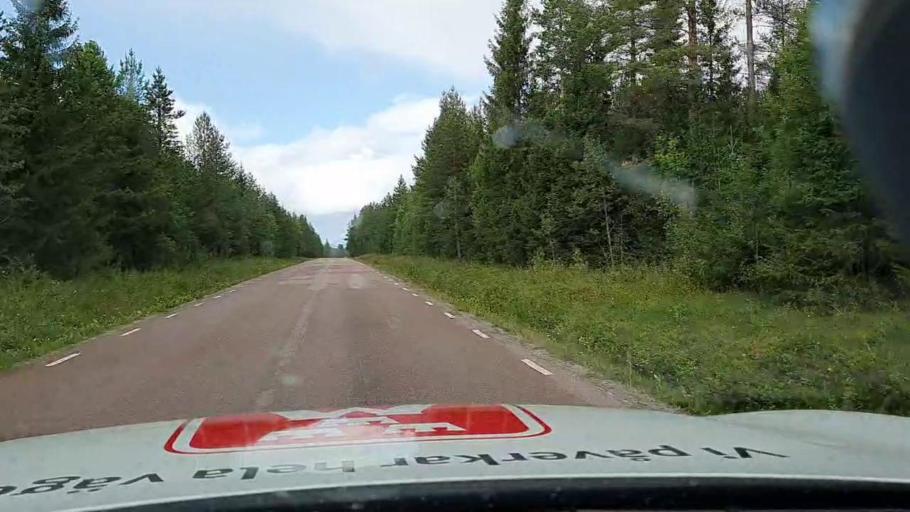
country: SE
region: Jaemtland
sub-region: Stroemsunds Kommun
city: Stroemsund
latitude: 63.8731
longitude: 15.3652
